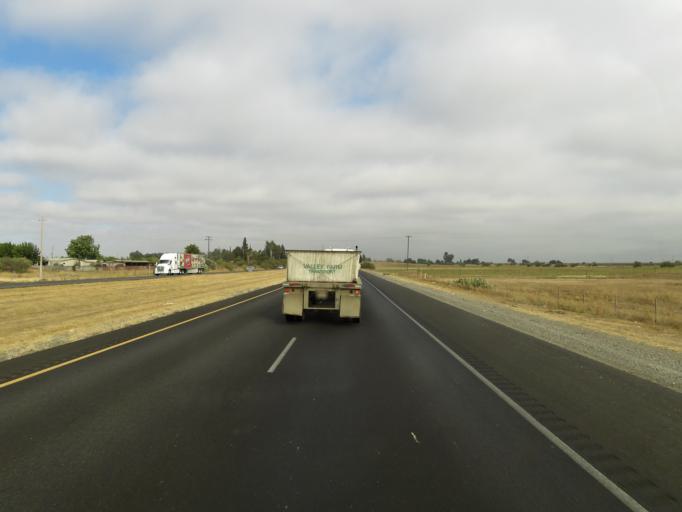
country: US
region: California
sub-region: Yolo County
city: Dunnigan
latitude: 38.9037
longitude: -121.9856
